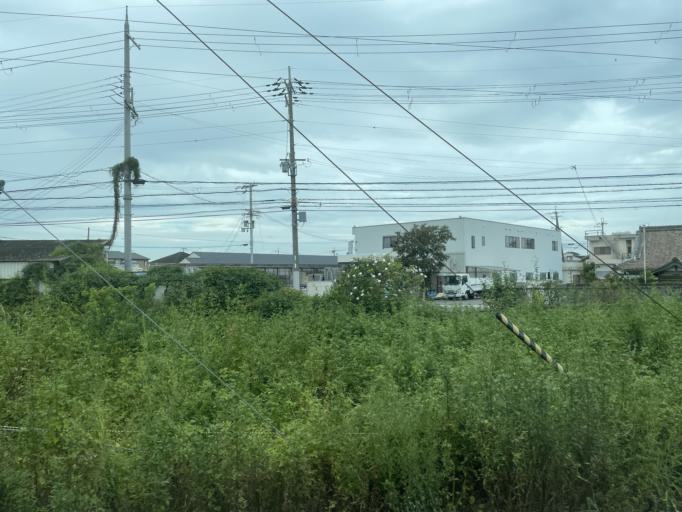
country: JP
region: Osaka
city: Kaizuka
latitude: 34.3830
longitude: 135.3216
